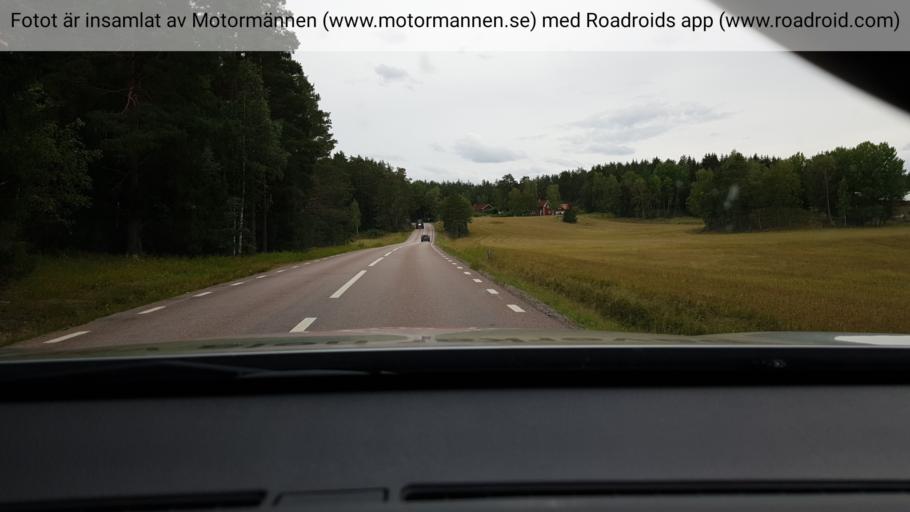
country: SE
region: Soedermanland
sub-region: Nykopings Kommun
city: Nykoping
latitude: 58.8528
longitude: 17.0595
